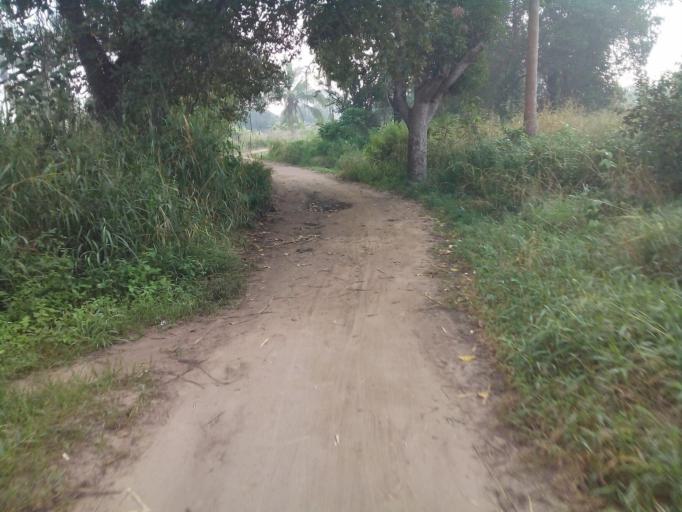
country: MZ
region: Zambezia
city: Quelimane
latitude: -17.5884
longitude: 36.6846
